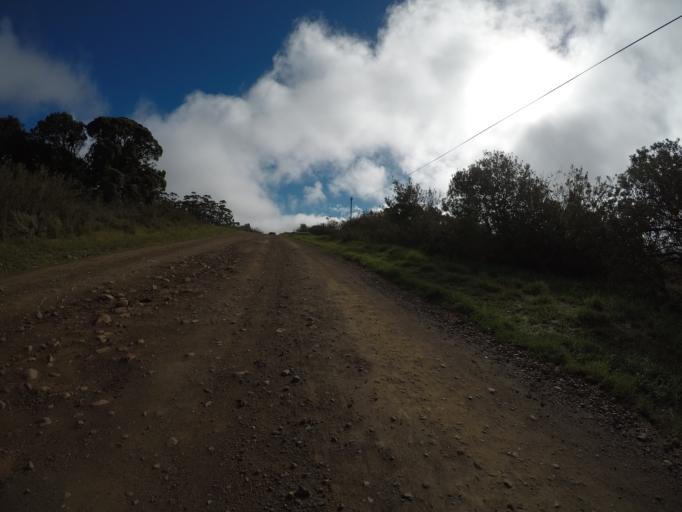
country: ZA
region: Western Cape
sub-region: Cape Winelands District Municipality
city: Ashton
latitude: -34.1233
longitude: 19.8097
